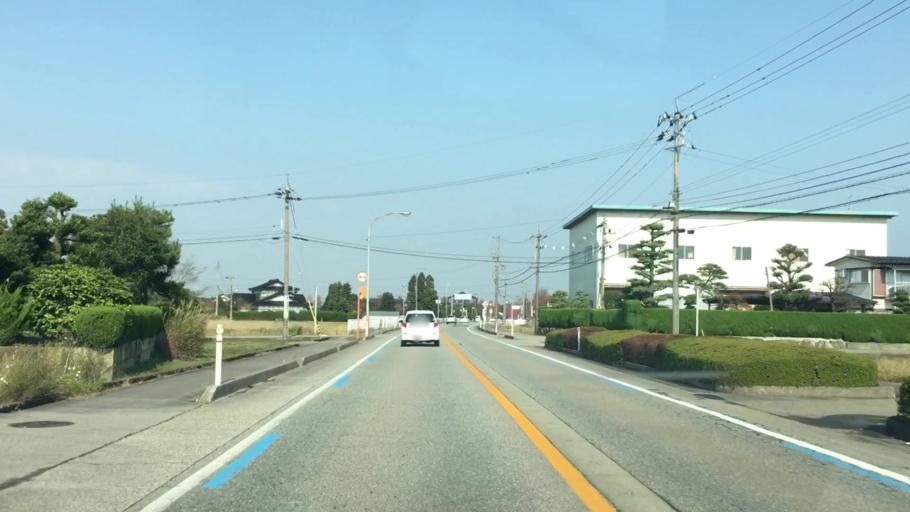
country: JP
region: Toyama
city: Toyama-shi
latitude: 36.6204
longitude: 137.1930
